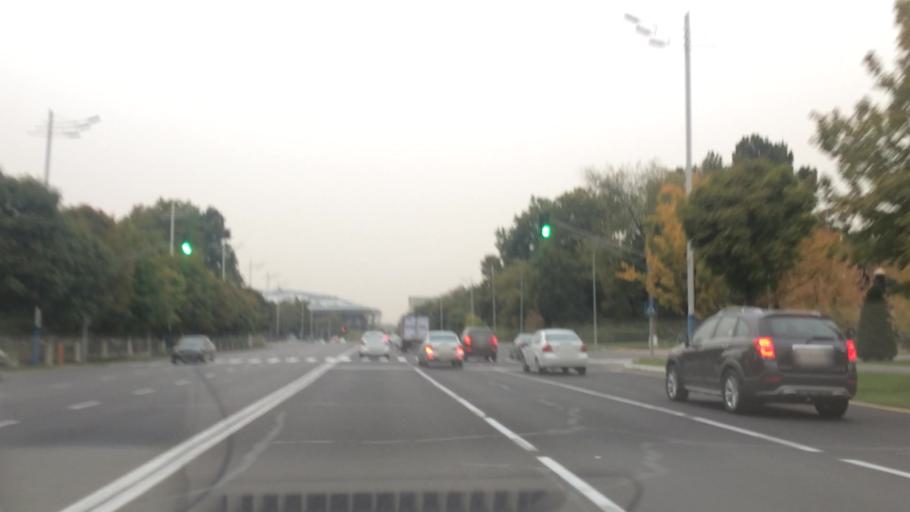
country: UZ
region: Toshkent Shahri
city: Tashkent
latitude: 41.3069
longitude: 69.2591
